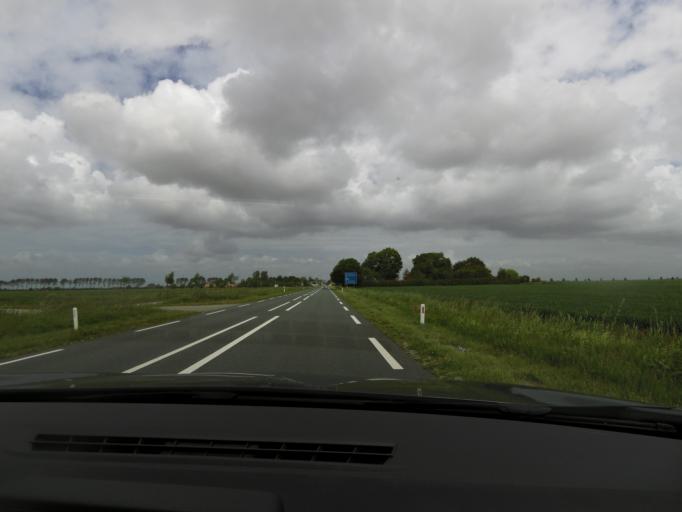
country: NL
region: Zeeland
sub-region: Schouwen-Duiveland
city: Scharendijke
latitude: 51.7039
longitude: 3.9459
